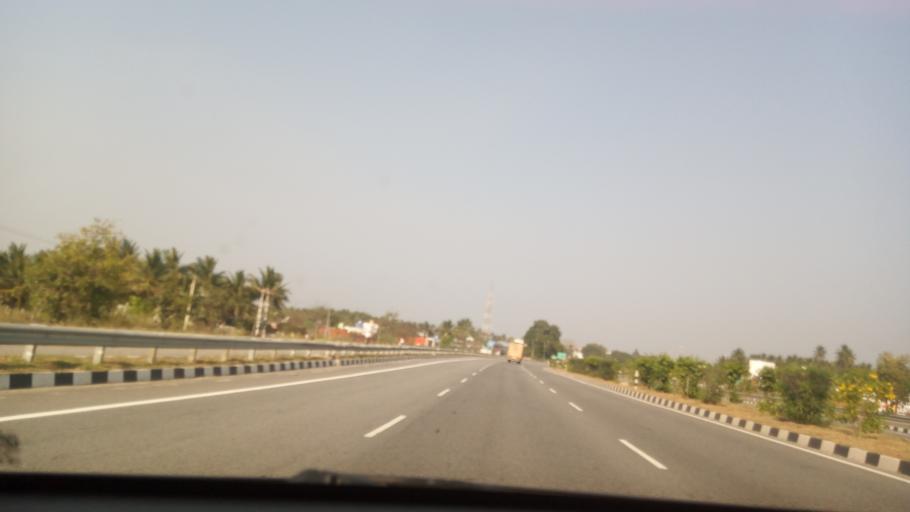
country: IN
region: Tamil Nadu
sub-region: Vellore
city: Jolarpettai
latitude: 12.5847
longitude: 78.5011
